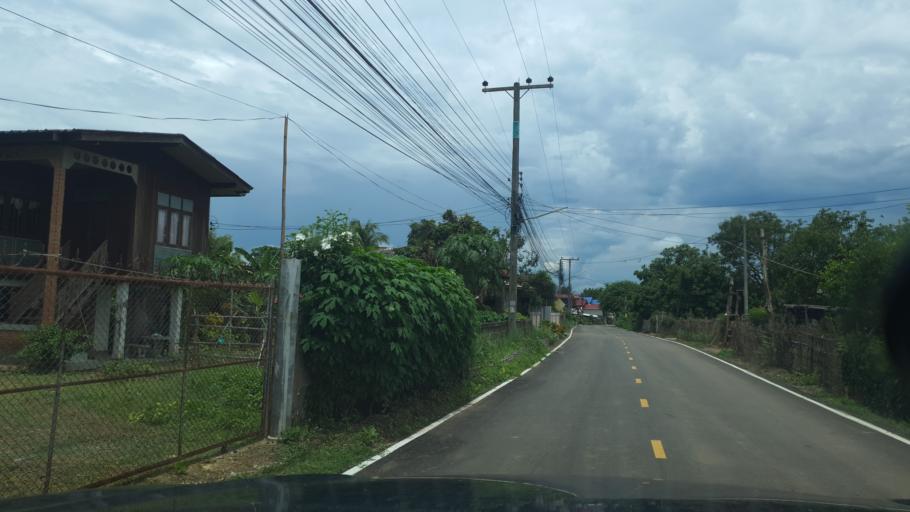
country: TH
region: Lampang
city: Ko Kha
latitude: 18.1986
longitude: 99.3324
